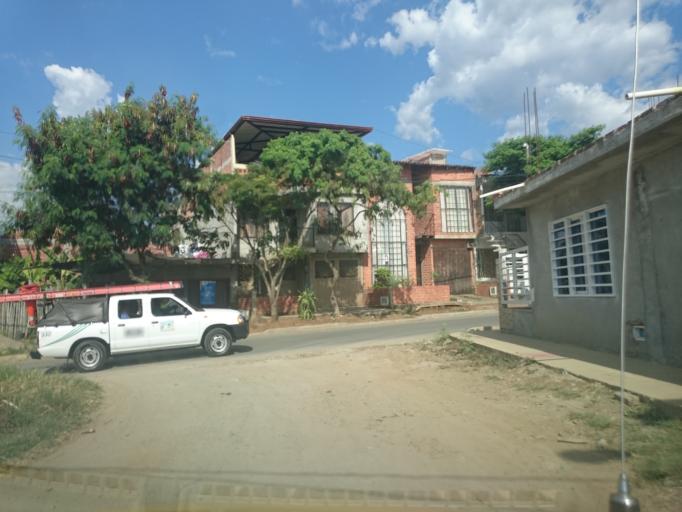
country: CO
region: Cauca
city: Santander de Quilichao
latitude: 3.0160
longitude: -76.4854
